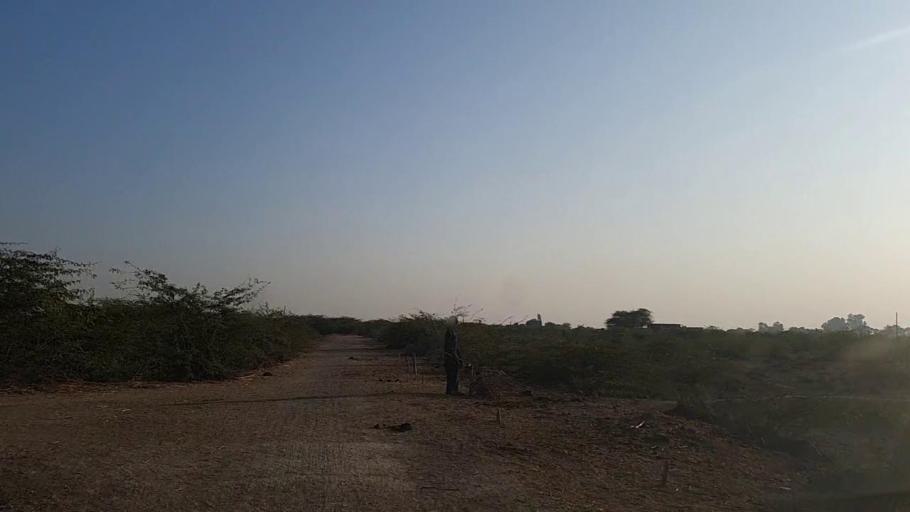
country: PK
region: Sindh
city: Naukot
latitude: 24.9256
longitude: 69.4370
